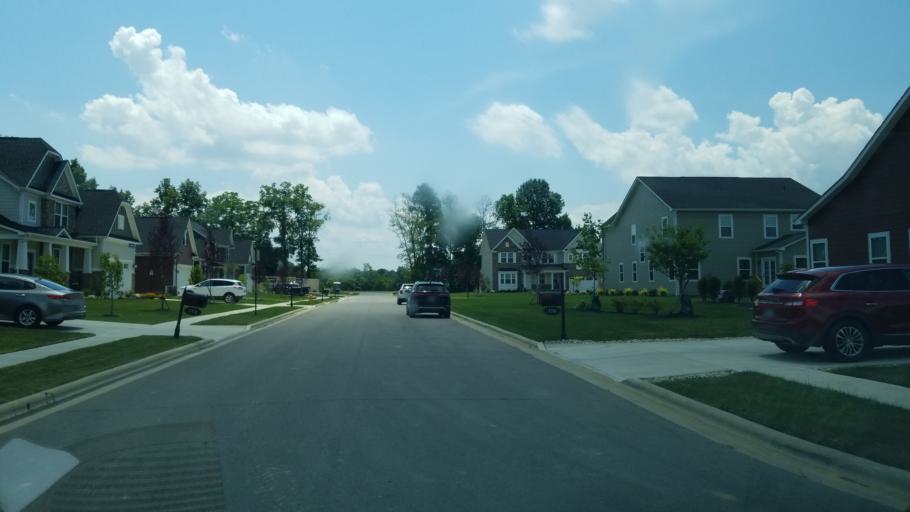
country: US
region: Ohio
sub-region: Delaware County
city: Sunbury
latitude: 40.2590
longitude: -82.9431
